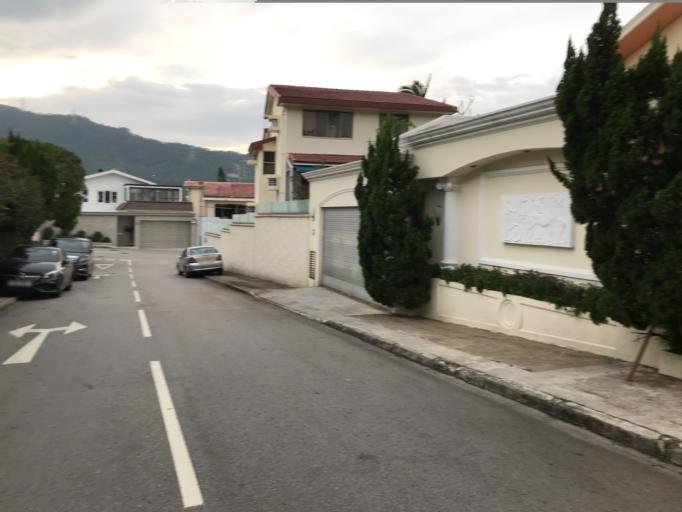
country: HK
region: Tai Po
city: Tai Po
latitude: 22.4617
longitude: 114.1537
